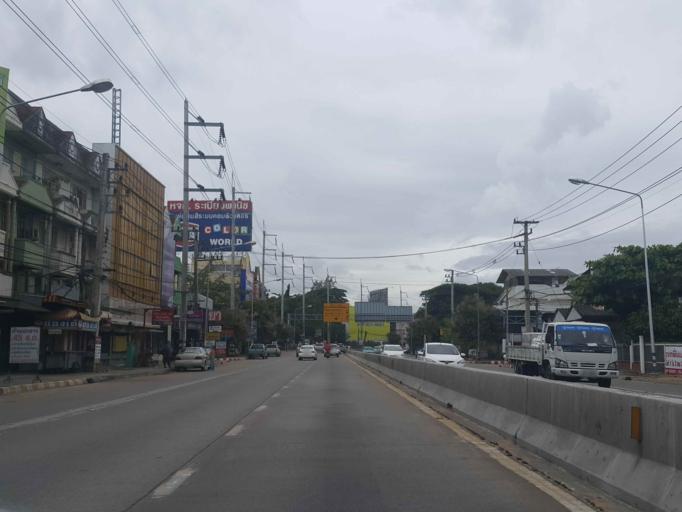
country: TH
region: Chiang Mai
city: Chiang Mai
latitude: 18.7571
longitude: 99.0035
